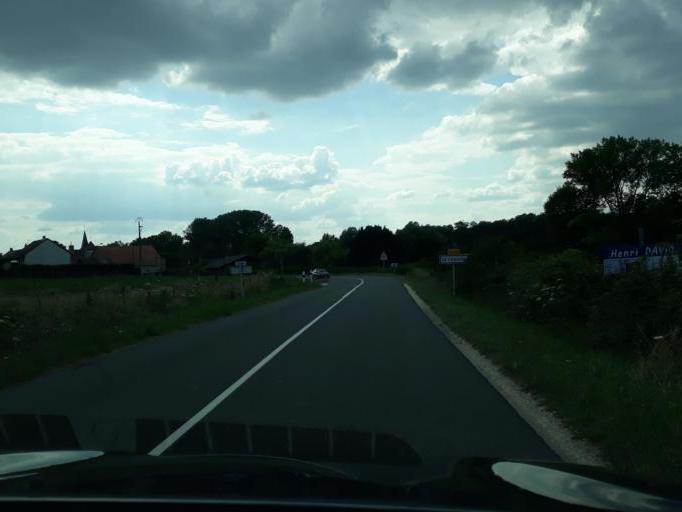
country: FR
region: Centre
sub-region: Departement du Cher
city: Jouet-sur-l'Aubois
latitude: 46.9784
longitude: 2.9701
